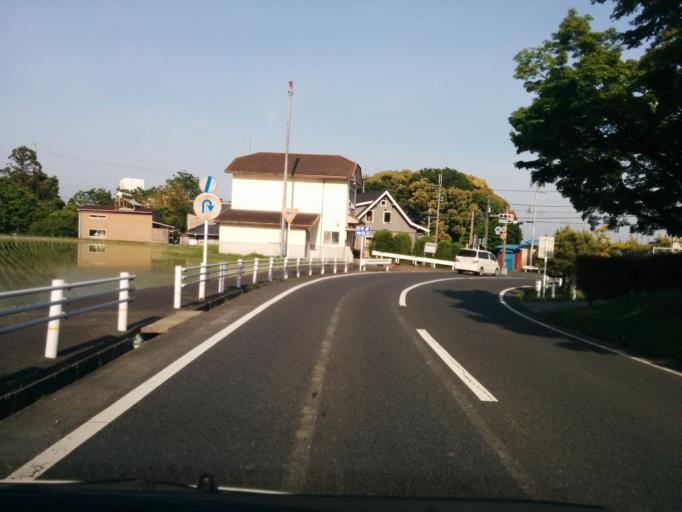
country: JP
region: Shiga Prefecture
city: Kitahama
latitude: 35.1079
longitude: 135.8807
